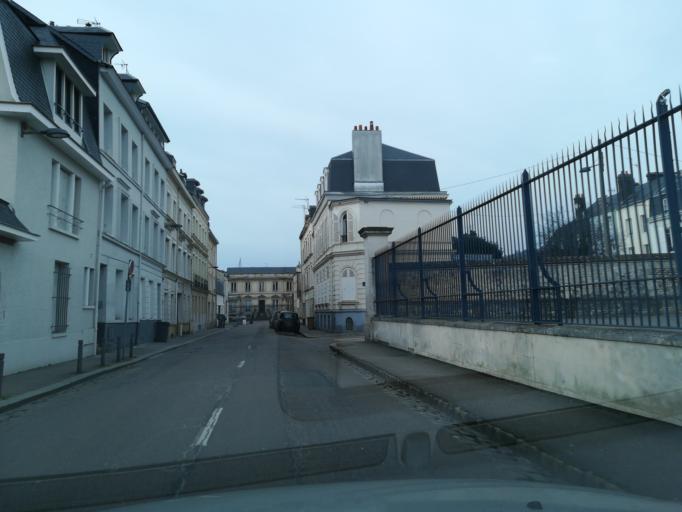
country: FR
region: Haute-Normandie
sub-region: Departement de la Seine-Maritime
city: Rouen
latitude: 49.4459
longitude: 1.0789
